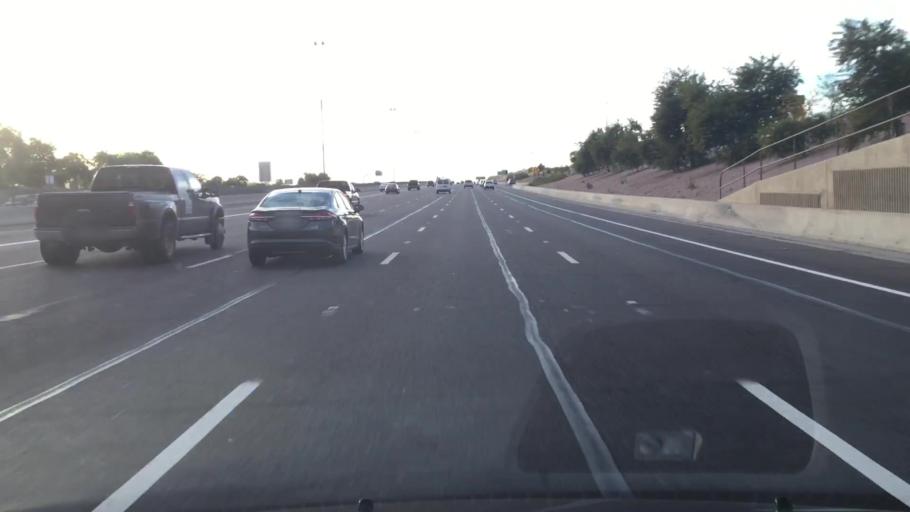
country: US
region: Arizona
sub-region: Maricopa County
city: Mesa
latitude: 33.3826
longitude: -111.8251
